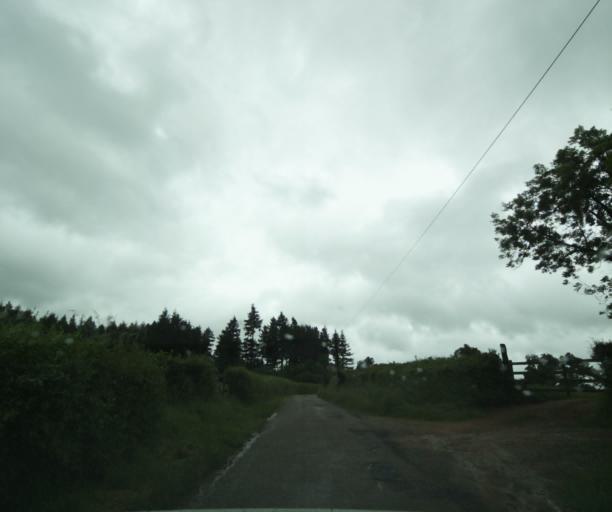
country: FR
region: Bourgogne
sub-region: Departement de Saone-et-Loire
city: Matour
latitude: 46.4663
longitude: 4.4734
